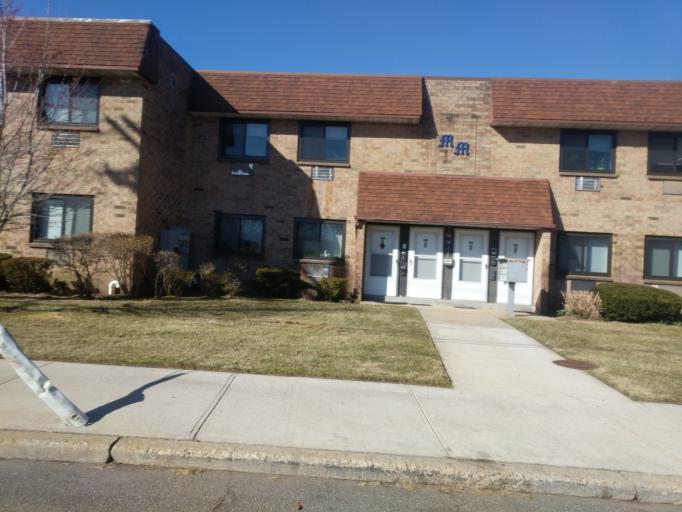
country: US
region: New York
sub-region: Nassau County
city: Inwood
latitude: 40.6126
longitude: -73.7453
